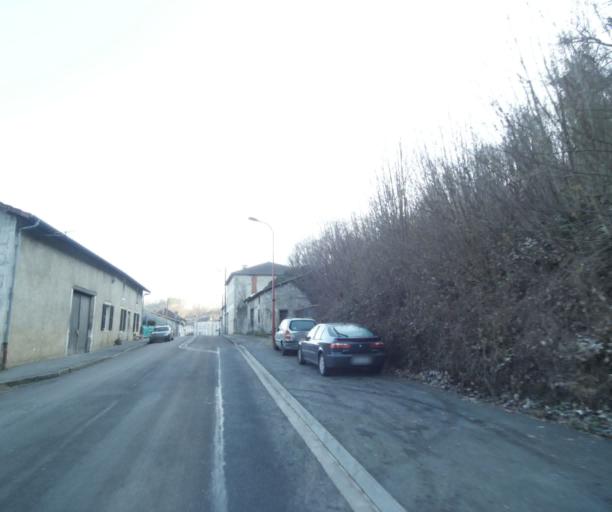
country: FR
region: Champagne-Ardenne
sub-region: Departement de la Haute-Marne
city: Bienville
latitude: 48.5503
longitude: 5.0708
